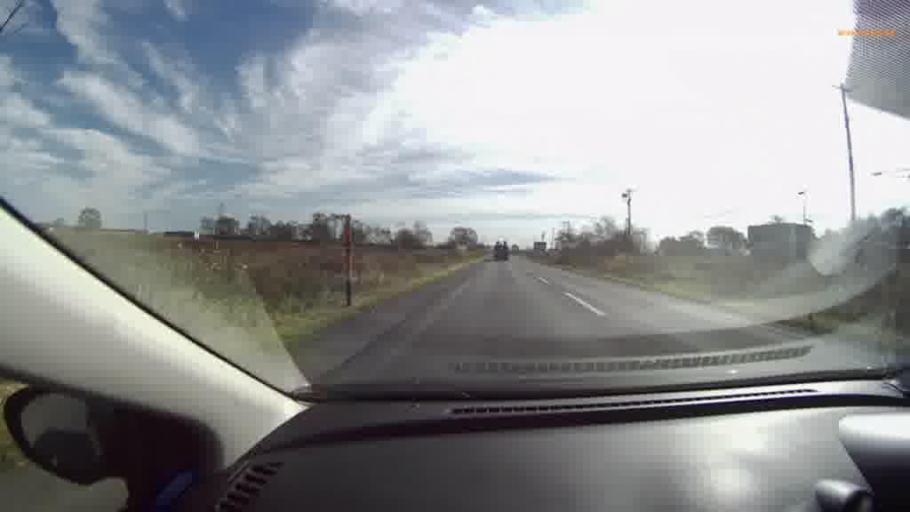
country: JP
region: Hokkaido
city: Kushiro
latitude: 43.0360
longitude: 144.2455
